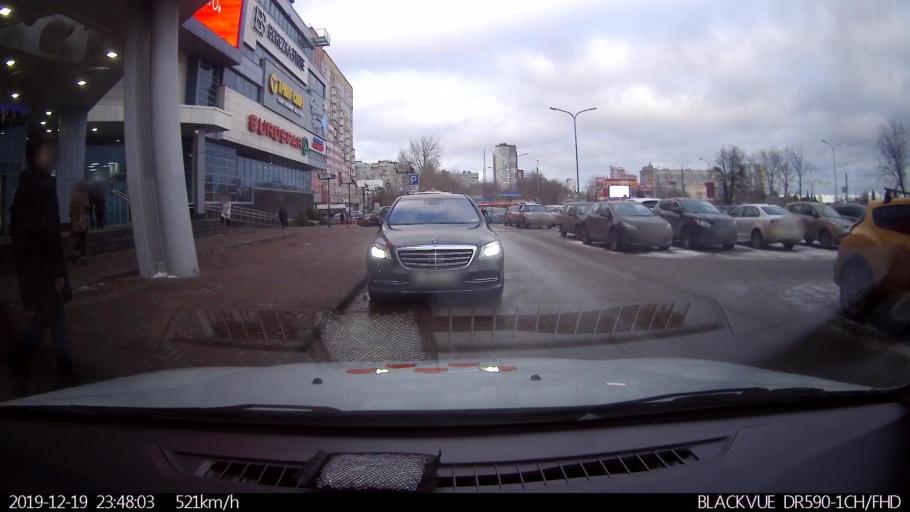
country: RU
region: Tverskaya
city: Ves'yegonsk
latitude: 58.7100
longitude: 37.6316
